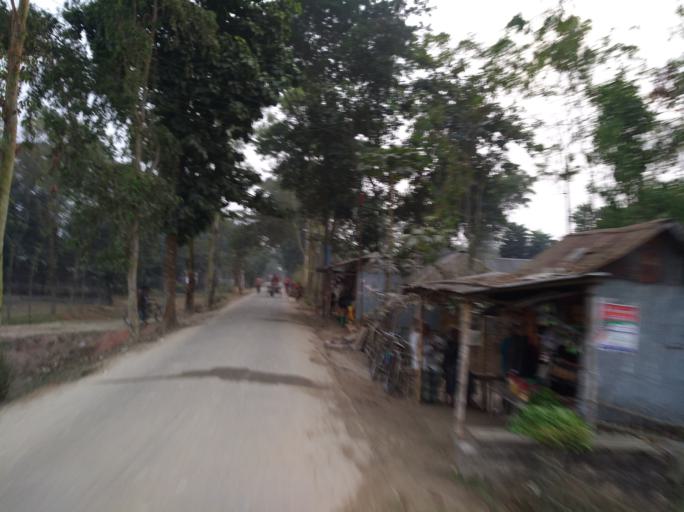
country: BD
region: Rajshahi
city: Saidpur
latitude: 25.9288
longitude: 88.8670
